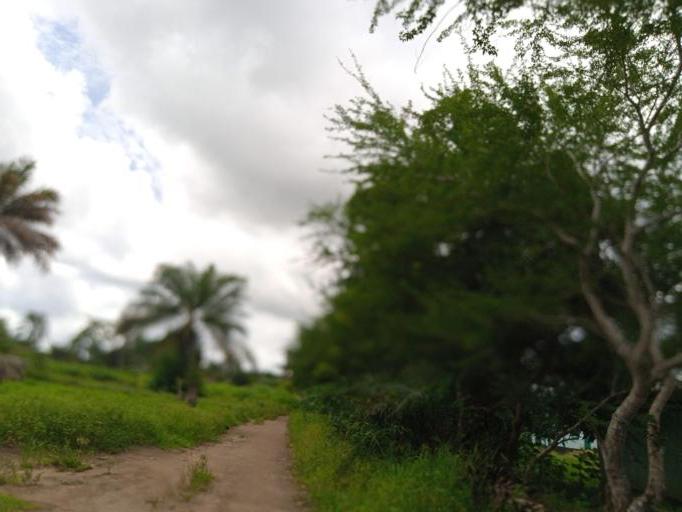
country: SL
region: Northern Province
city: Masoyila
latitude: 8.5885
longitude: -13.1680
